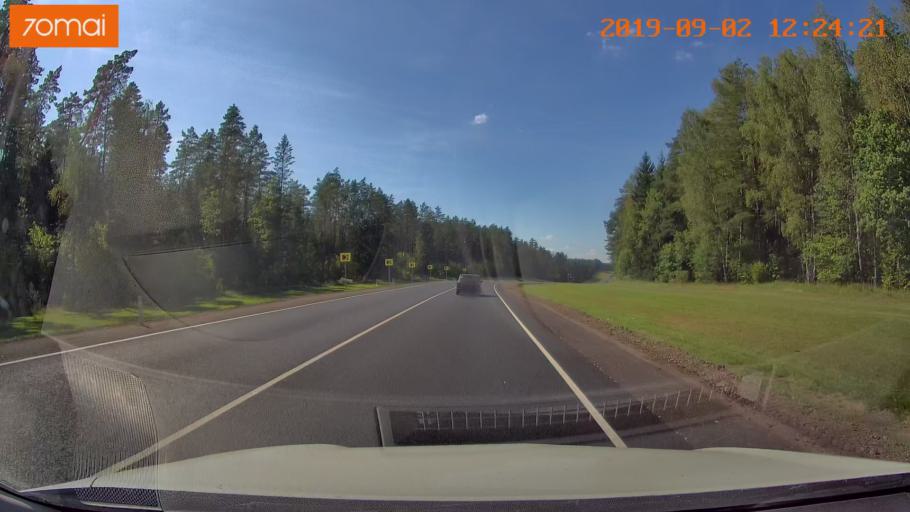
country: RU
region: Smolensk
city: Shumyachi
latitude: 53.8689
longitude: 32.6097
